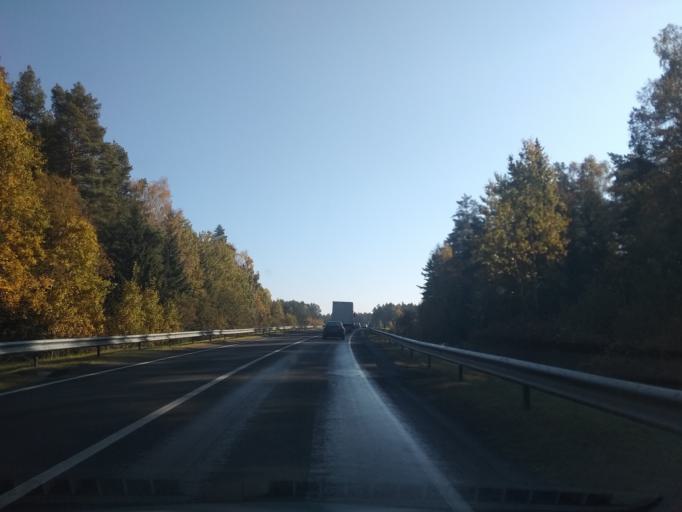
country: BY
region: Brest
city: Baranovichi
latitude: 53.0491
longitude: 25.8402
